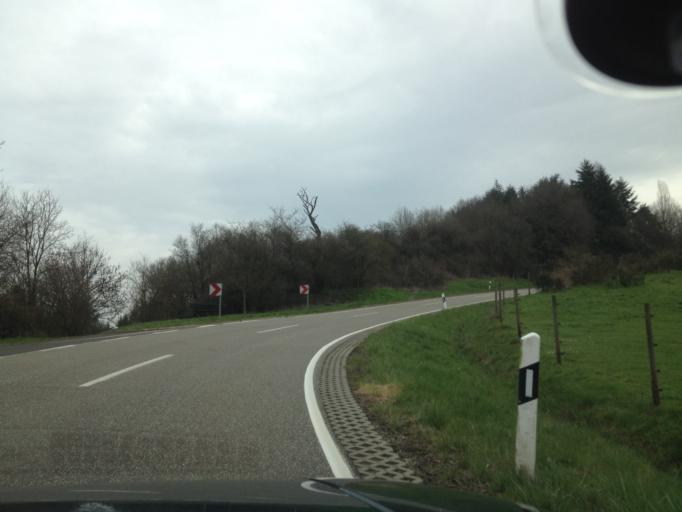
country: DE
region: Rheinland-Pfalz
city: Thallichtenberg
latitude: 49.5586
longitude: 7.3564
